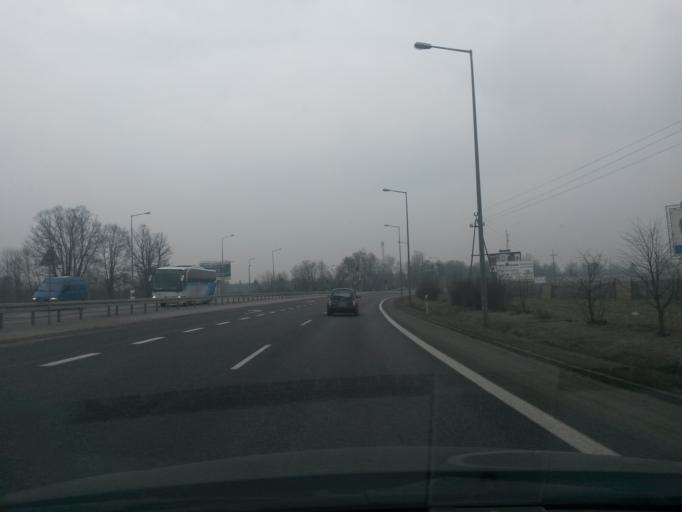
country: PL
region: Masovian Voivodeship
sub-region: Powiat legionowski
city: Bialobrzegi
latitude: 52.4705
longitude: 21.0294
